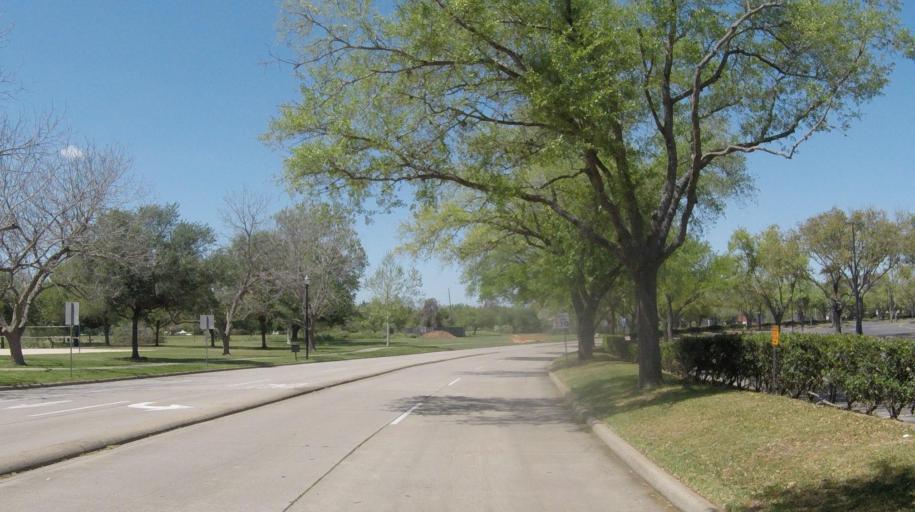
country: US
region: Texas
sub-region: Fort Bend County
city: Sugar Land
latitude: 29.6042
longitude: -95.6286
